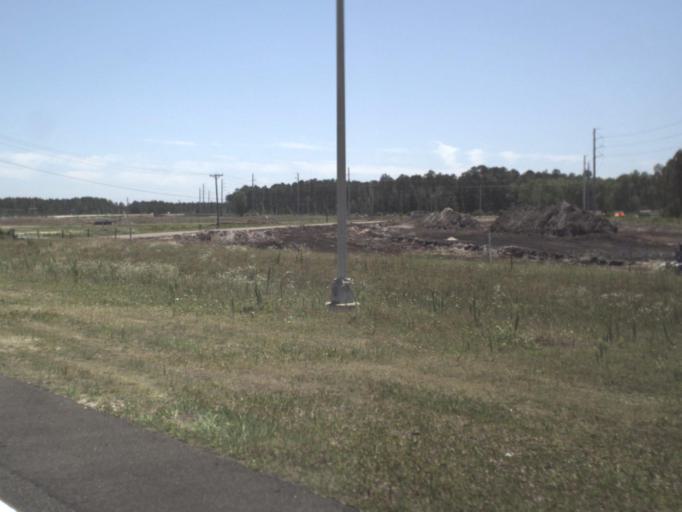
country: US
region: Florida
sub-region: Clay County
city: Bellair-Meadowbrook Terrace
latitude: 30.2517
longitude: -81.8493
